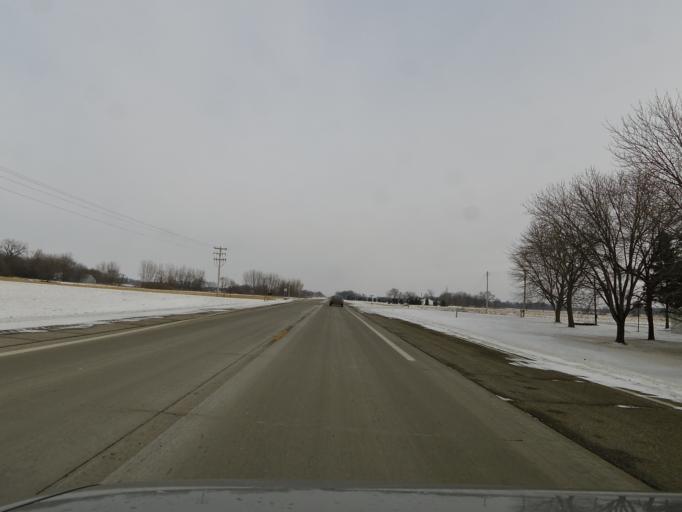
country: US
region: Minnesota
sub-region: McLeod County
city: Hutchinson
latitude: 44.8926
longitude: -94.3057
